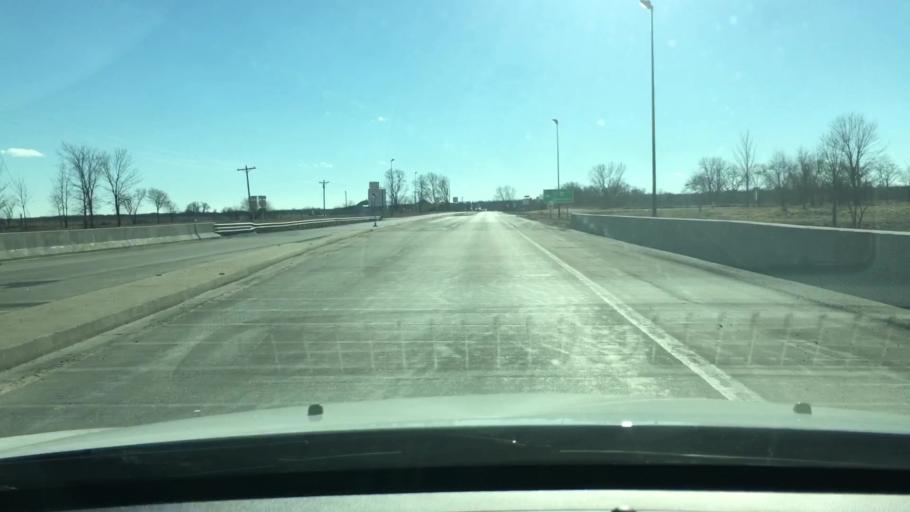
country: US
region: Illinois
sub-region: Pike County
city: Griggsville
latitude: 39.6741
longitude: -90.7687
